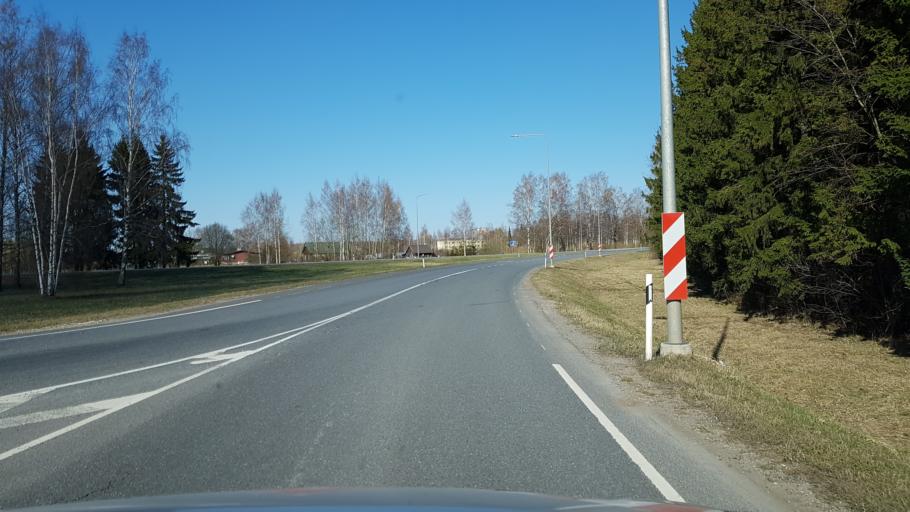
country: EE
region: Tartu
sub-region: Tartu linn
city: Tartu
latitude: 58.4092
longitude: 26.7091
